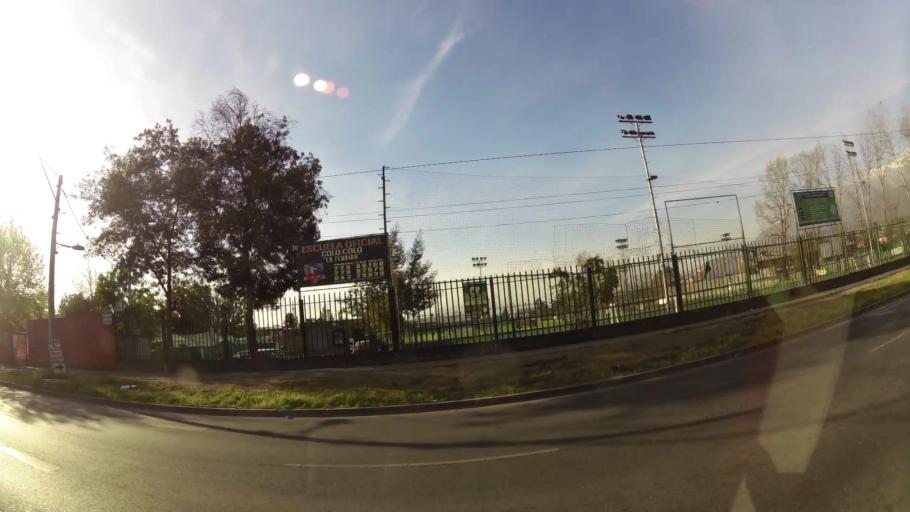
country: CL
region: Santiago Metropolitan
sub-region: Provincia de Cordillera
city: Puente Alto
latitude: -33.5530
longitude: -70.5763
